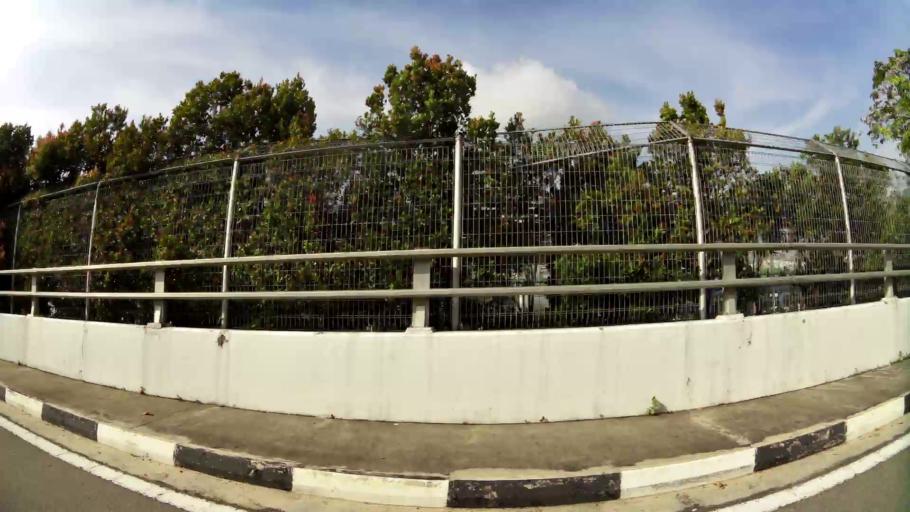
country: SG
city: Singapore
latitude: 1.2539
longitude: 103.8254
